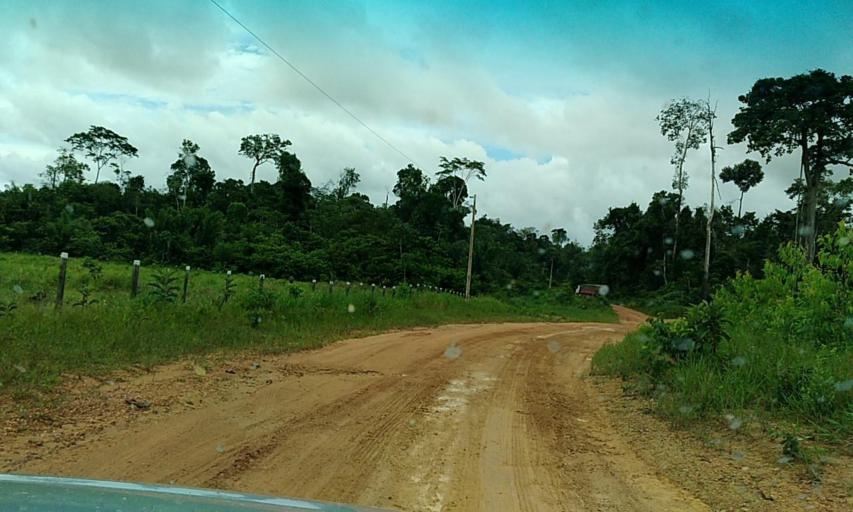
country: BR
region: Para
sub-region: Altamira
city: Altamira
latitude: -3.0471
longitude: -51.7267
